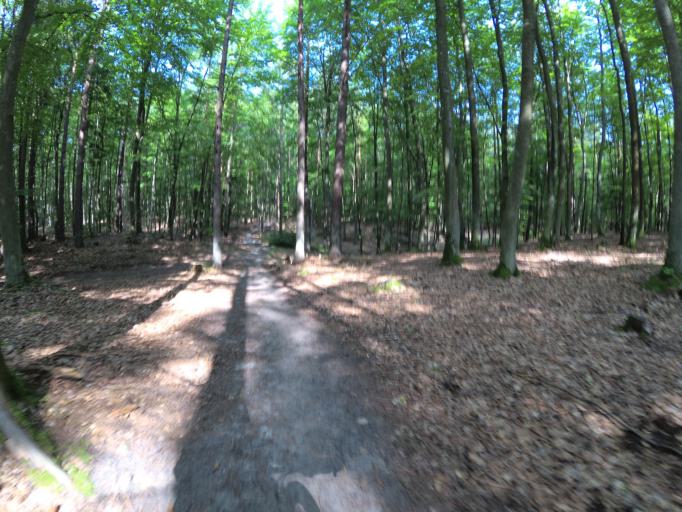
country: PL
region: Pomeranian Voivodeship
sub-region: Gdynia
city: Wielki Kack
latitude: 54.4966
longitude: 18.4799
